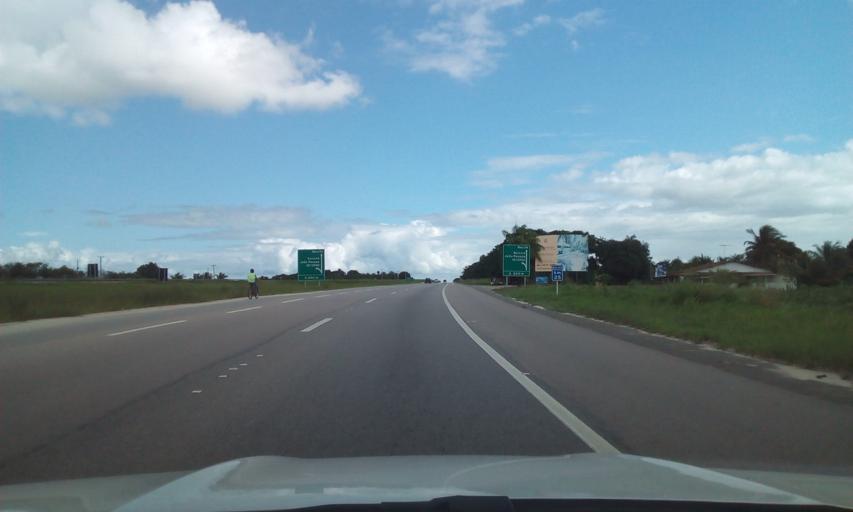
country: BR
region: Pernambuco
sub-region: Itapissuma
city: Itapissuma
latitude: -7.7002
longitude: -34.9225
